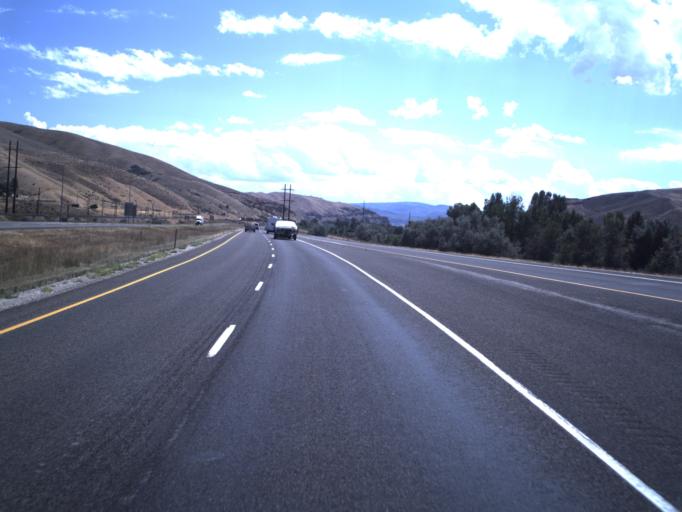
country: US
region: Utah
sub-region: Summit County
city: Coalville
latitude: 41.0141
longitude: -111.4884
